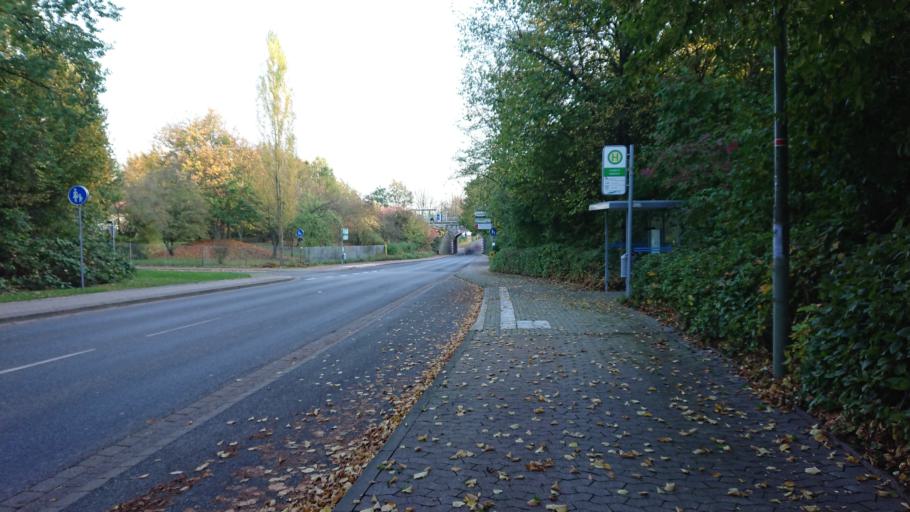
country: DE
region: Lower Saxony
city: Bovenden
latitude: 51.5895
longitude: 9.8705
